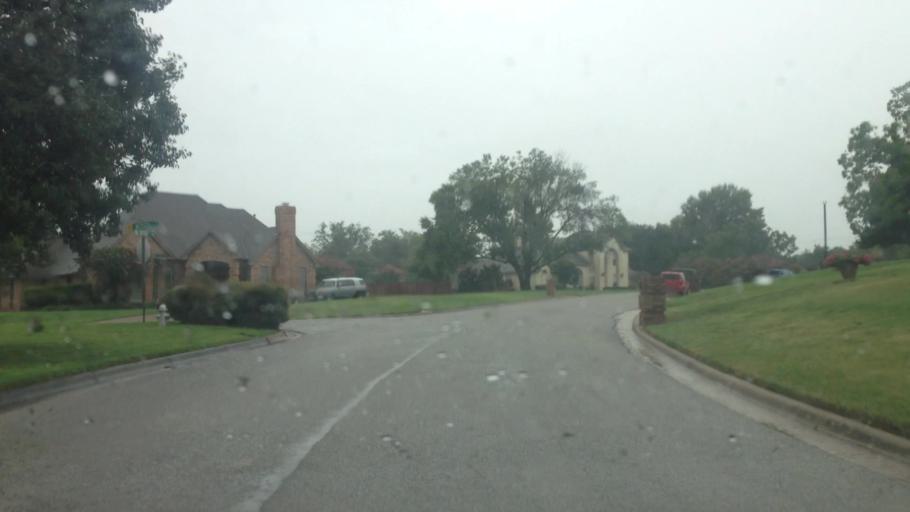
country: US
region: Texas
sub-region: Denton County
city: Trophy Club
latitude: 32.9502
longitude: -97.1970
